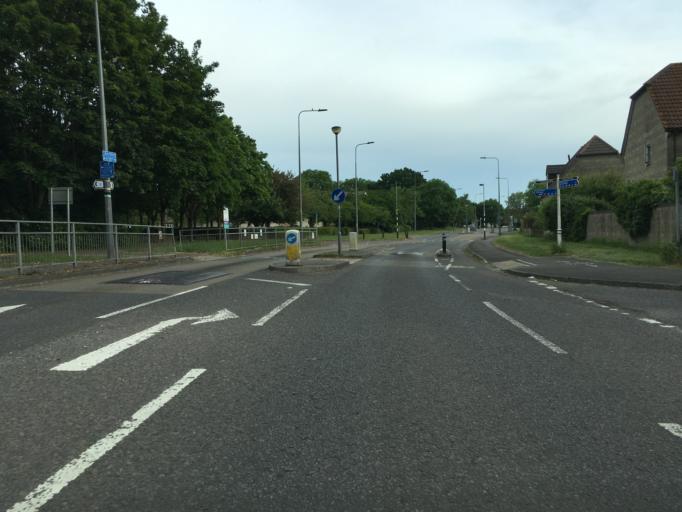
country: GB
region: England
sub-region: South Gloucestershire
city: Almondsbury
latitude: 51.5392
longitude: -2.5600
